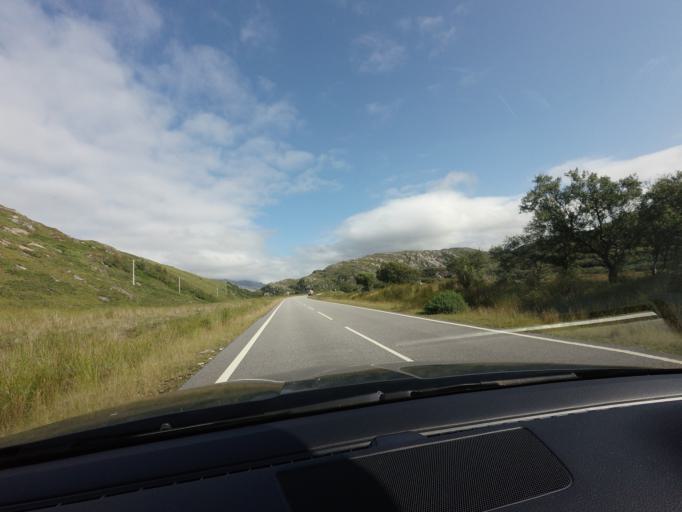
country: GB
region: Scotland
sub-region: Highland
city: Ullapool
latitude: 58.3779
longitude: -5.0207
